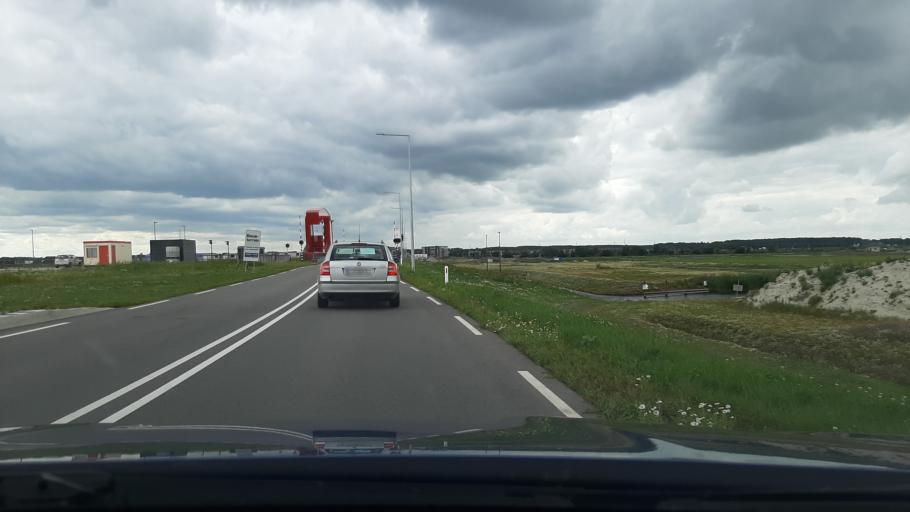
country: NL
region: Flevoland
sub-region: Gemeente Zeewolde
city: Zeewolde
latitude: 52.3523
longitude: 5.5349
